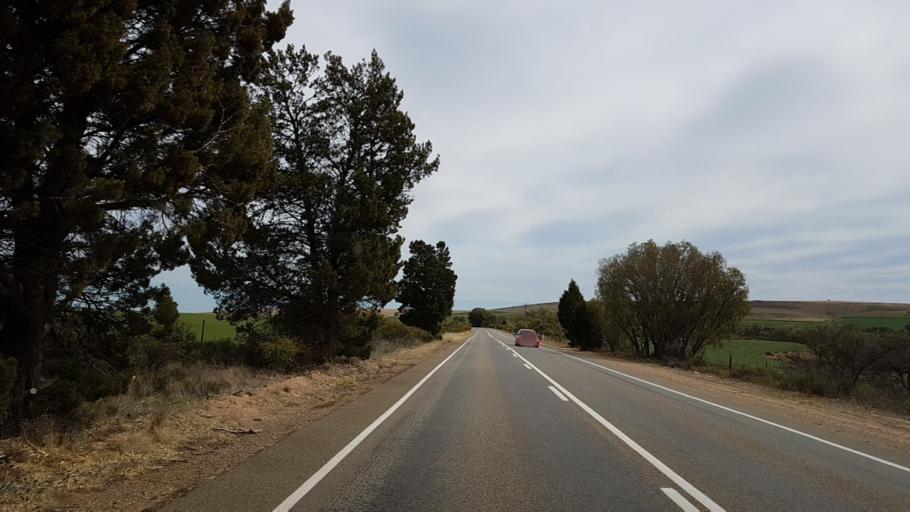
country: AU
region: South Australia
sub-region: Northern Areas
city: Jamestown
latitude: -33.2263
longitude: 138.3998
